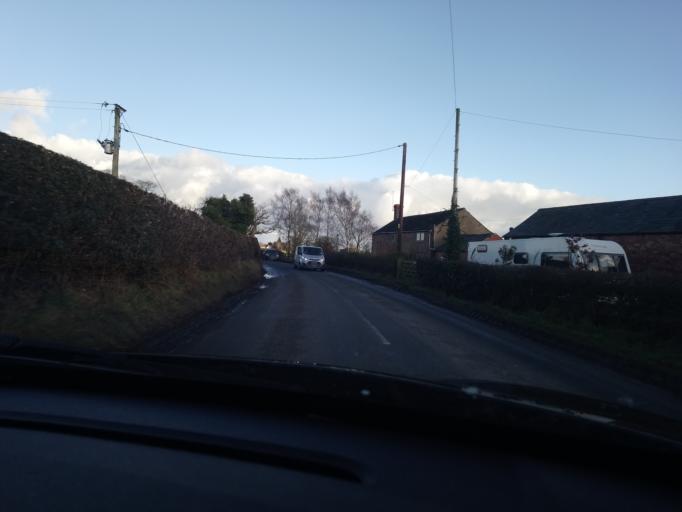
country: GB
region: England
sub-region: Shropshire
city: Petton
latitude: 52.8997
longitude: -2.8072
